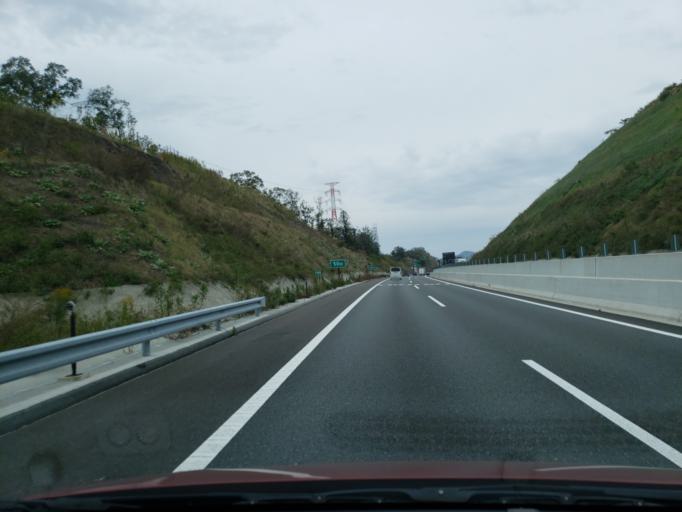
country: JP
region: Hyogo
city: Sandacho
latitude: 34.8623
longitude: 135.2578
